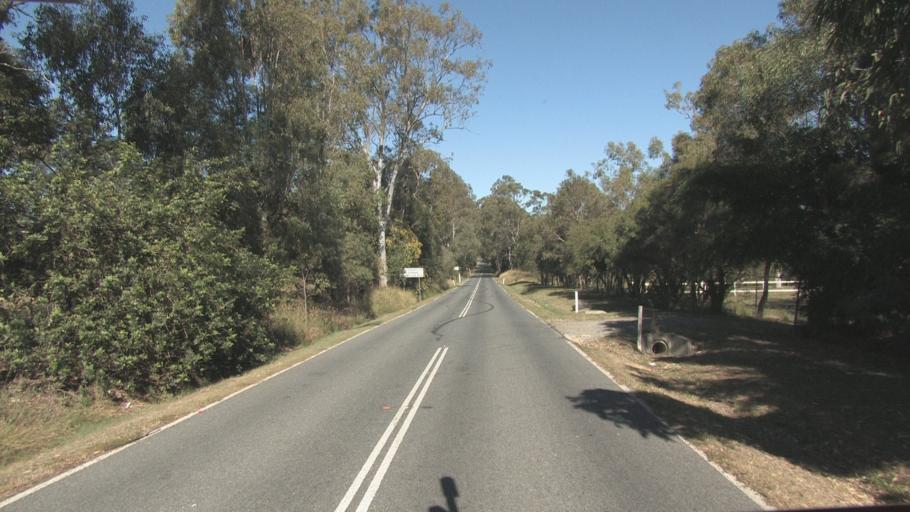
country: AU
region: Queensland
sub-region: Logan
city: Waterford West
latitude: -27.7126
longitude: 153.1410
